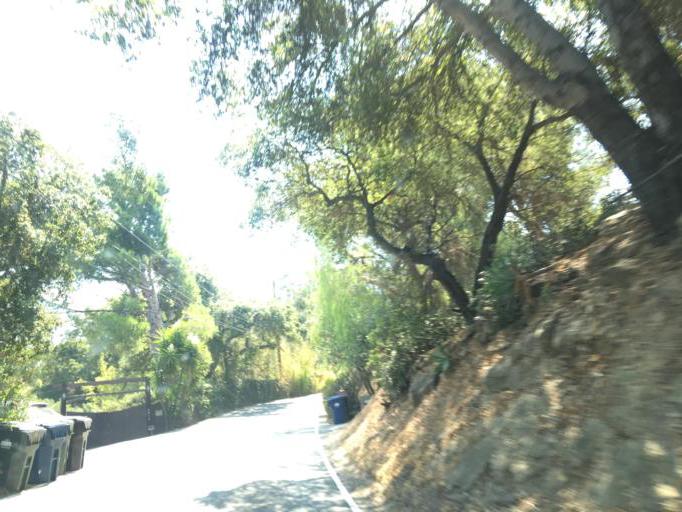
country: US
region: California
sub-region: Los Angeles County
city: Topanga
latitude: 34.0723
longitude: -118.6063
